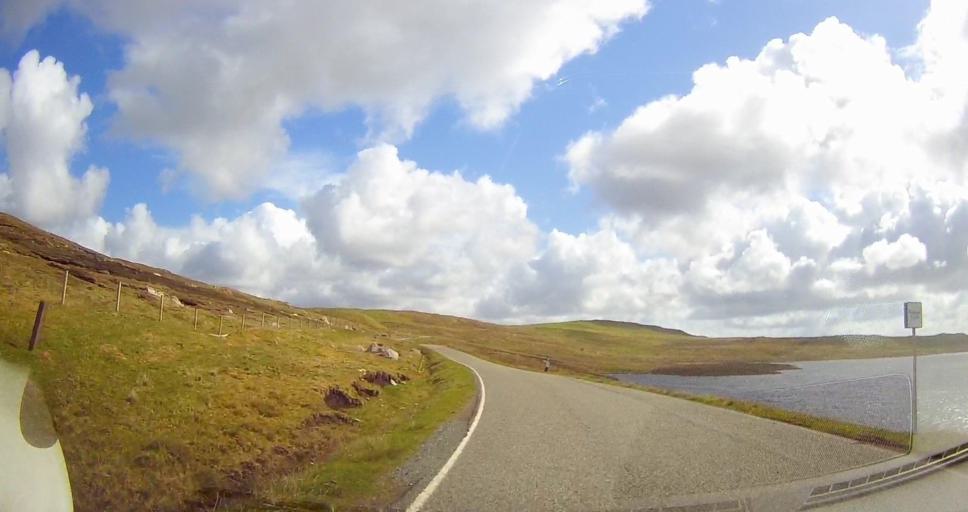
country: GB
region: Scotland
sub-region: Shetland Islands
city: Lerwick
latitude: 60.4933
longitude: -1.3917
